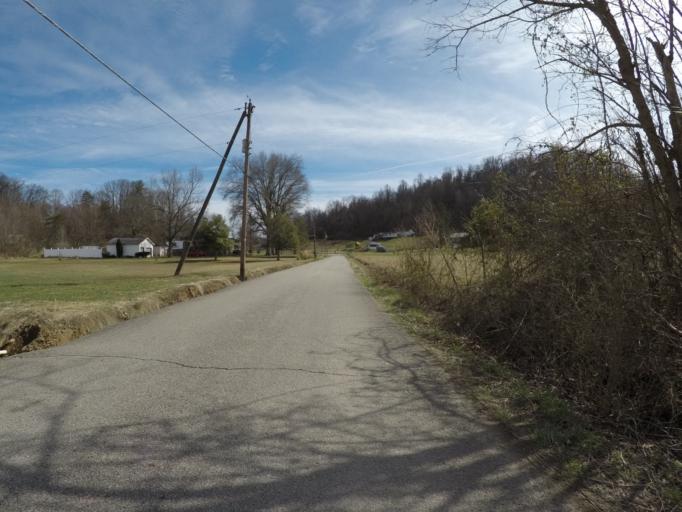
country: US
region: Ohio
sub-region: Lawrence County
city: Burlington
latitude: 38.3500
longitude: -82.5105
